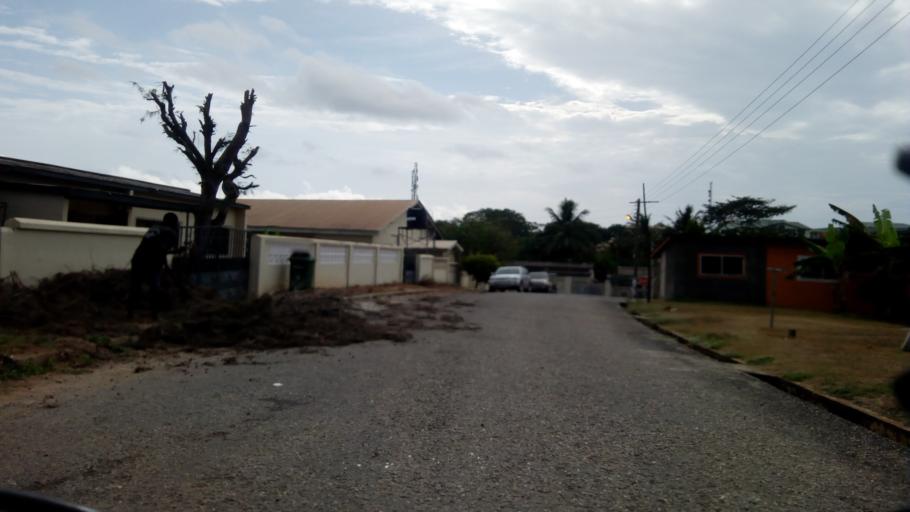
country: GH
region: Central
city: Cape Coast
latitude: 5.1049
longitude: -1.2767
